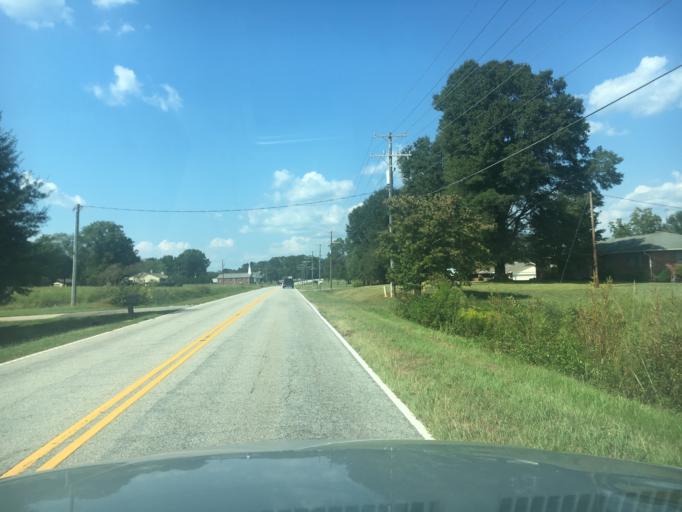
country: US
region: South Carolina
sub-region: Anderson County
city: Pendleton
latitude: 34.5758
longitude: -82.8082
